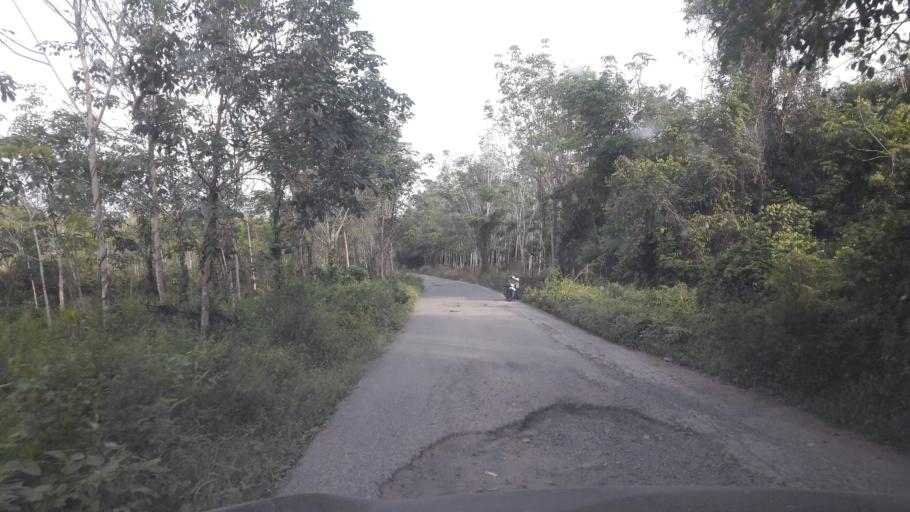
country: ID
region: South Sumatra
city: Gunungmenang
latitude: -3.2720
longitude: 104.0771
